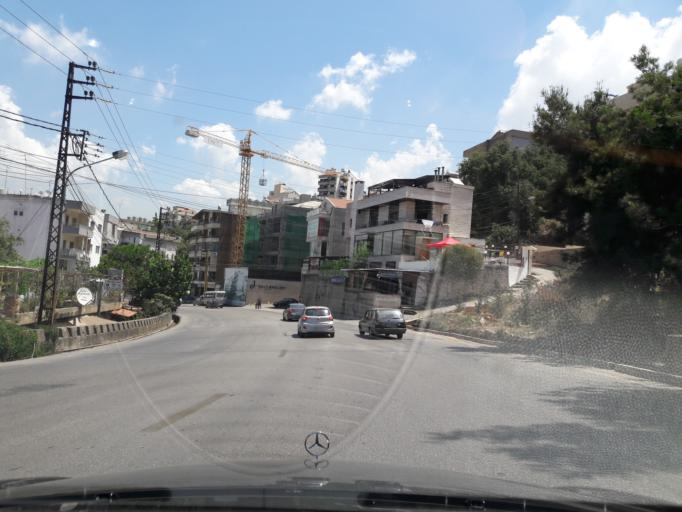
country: LB
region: Mont-Liban
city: Djounie
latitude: 33.9234
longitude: 35.6333
